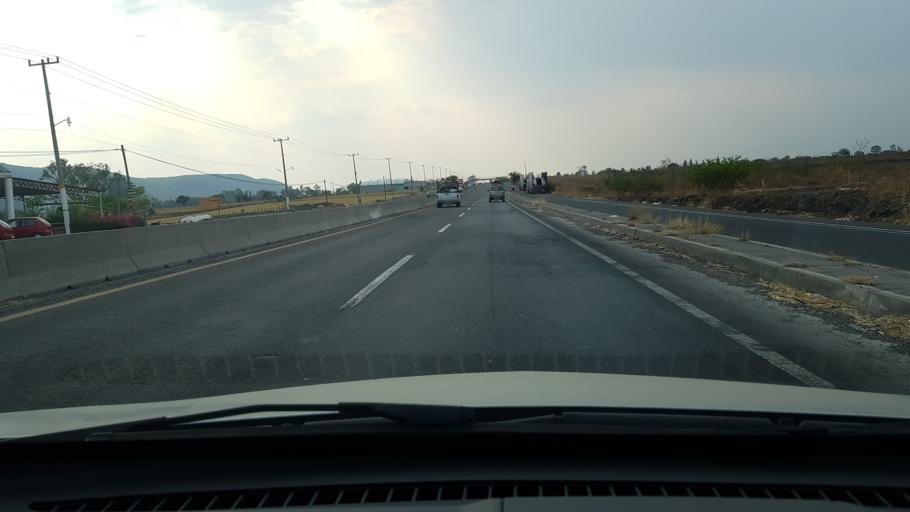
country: MX
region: Morelos
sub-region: Ayala
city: Unidad Habitacional Mariano Matamoros
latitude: 18.7404
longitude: -98.8306
